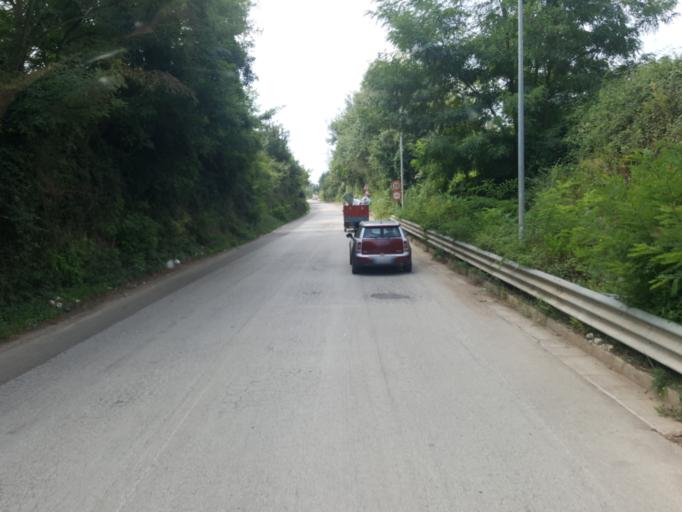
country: IT
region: Campania
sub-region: Provincia di Caserta
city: Pignataro Maggiore
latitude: 41.1769
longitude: 14.1528
